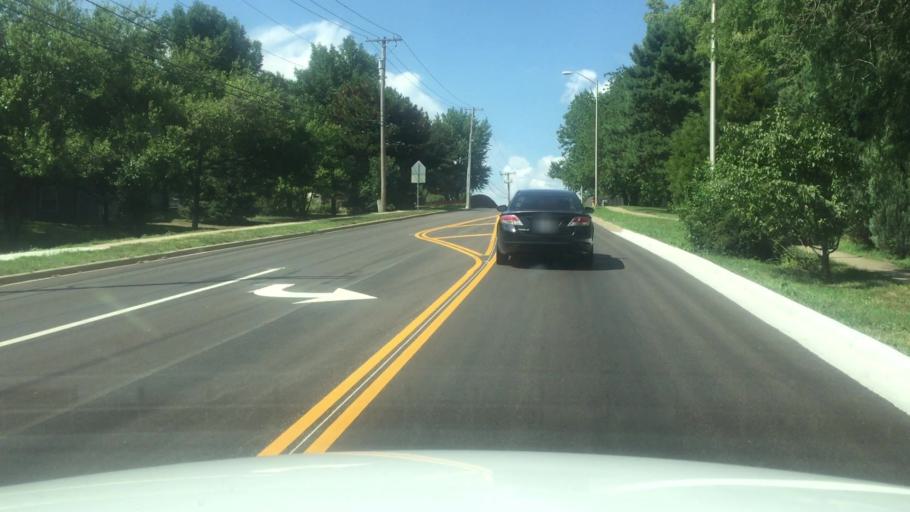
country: US
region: Kansas
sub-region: Johnson County
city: Lenexa
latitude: 38.9787
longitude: -94.7423
